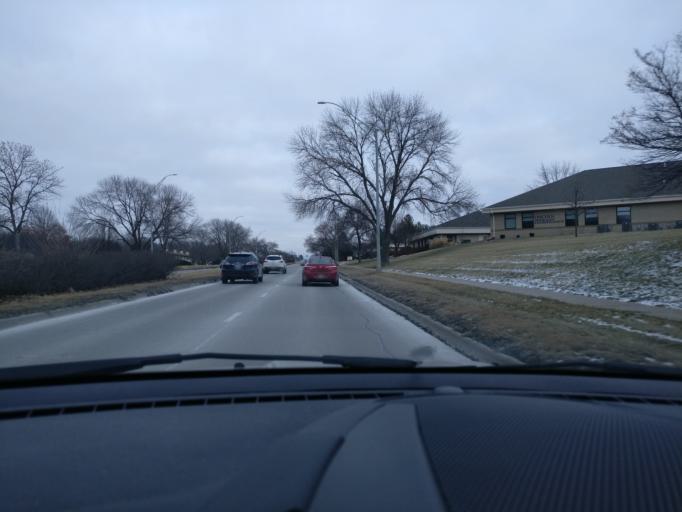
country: US
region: Nebraska
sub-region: Lancaster County
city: Lincoln
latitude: 40.8133
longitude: -96.6203
